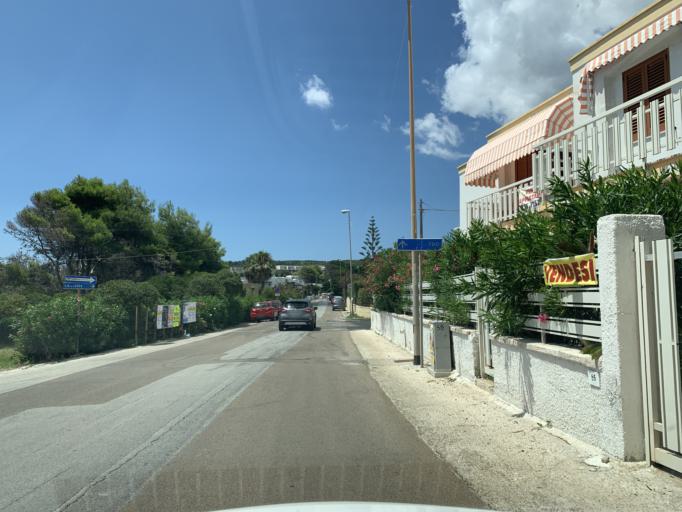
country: IT
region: Apulia
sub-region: Provincia di Lecce
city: Santa Cesarea Terme
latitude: 40.0352
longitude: 18.4562
